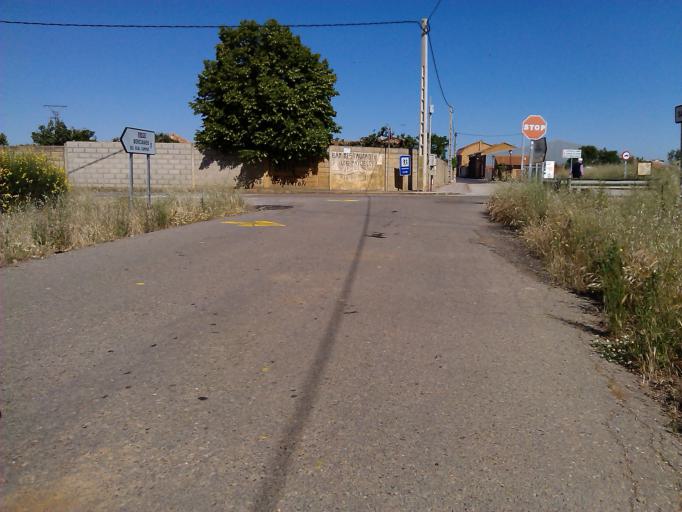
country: ES
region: Castille and Leon
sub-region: Provincia de Leon
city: Vallecillo
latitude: 42.4199
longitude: -5.2151
